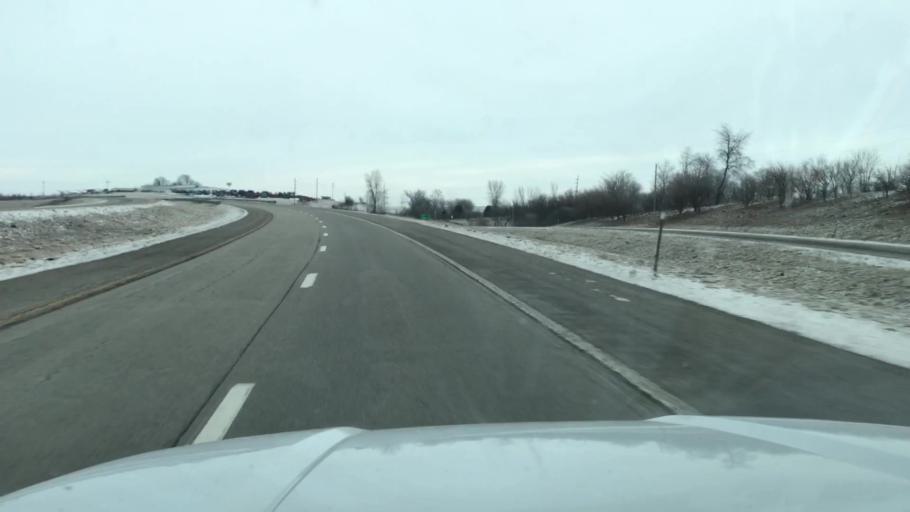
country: US
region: Missouri
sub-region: Andrew County
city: Savannah
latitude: 39.9587
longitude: -94.8601
